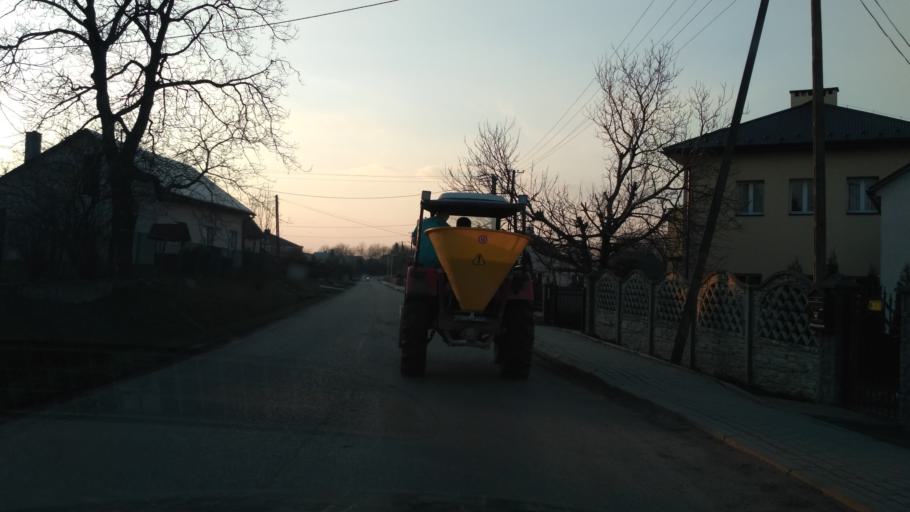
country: PL
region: Subcarpathian Voivodeship
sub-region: Powiat przeworski
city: Zarzecze
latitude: 49.9674
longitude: 22.5564
